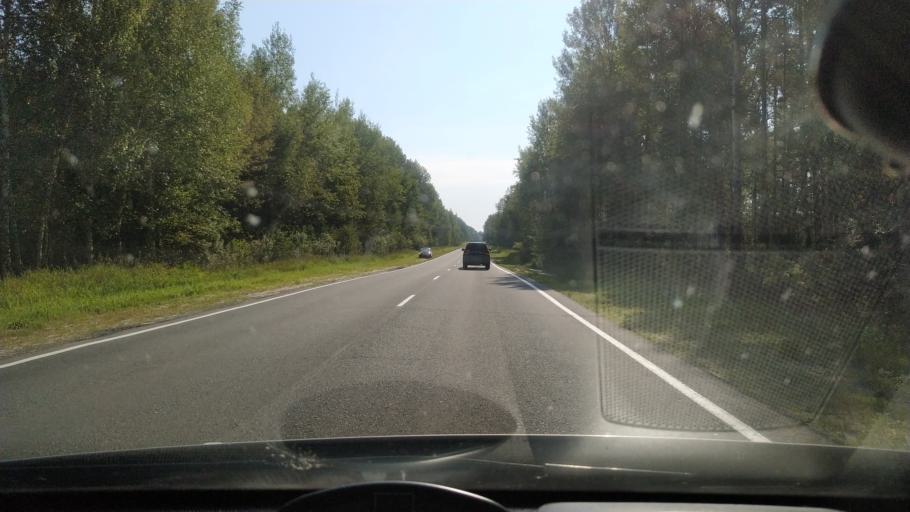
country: RU
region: Rjazan
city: Spas-Klepiki
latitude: 55.2229
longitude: 40.0762
